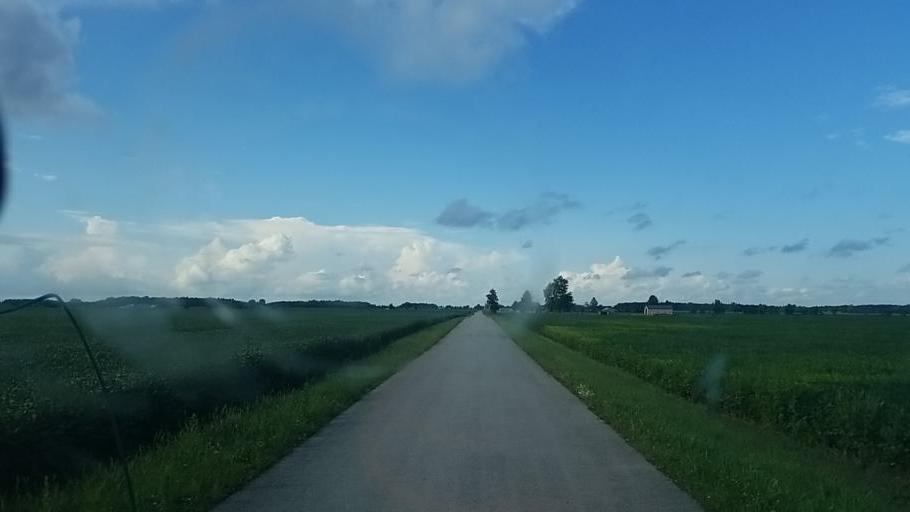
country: US
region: Ohio
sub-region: Hardin County
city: Forest
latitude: 40.7635
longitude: -83.4488
